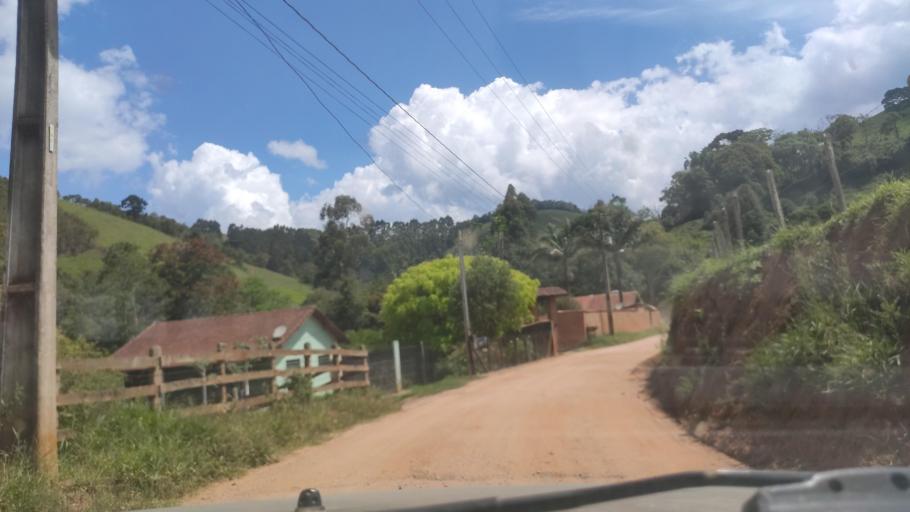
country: BR
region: Minas Gerais
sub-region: Cambui
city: Cambui
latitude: -22.7091
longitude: -46.0355
